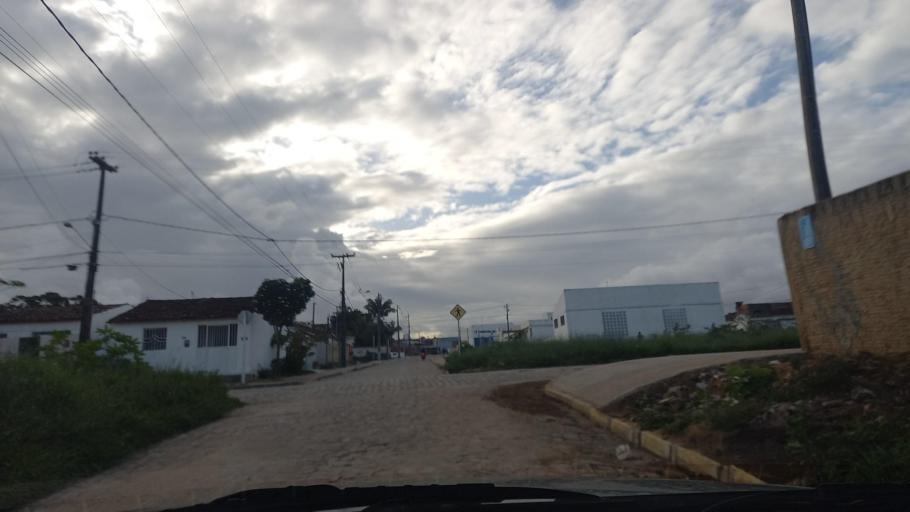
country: BR
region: Pernambuco
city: Garanhuns
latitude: -8.9117
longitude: -36.4844
